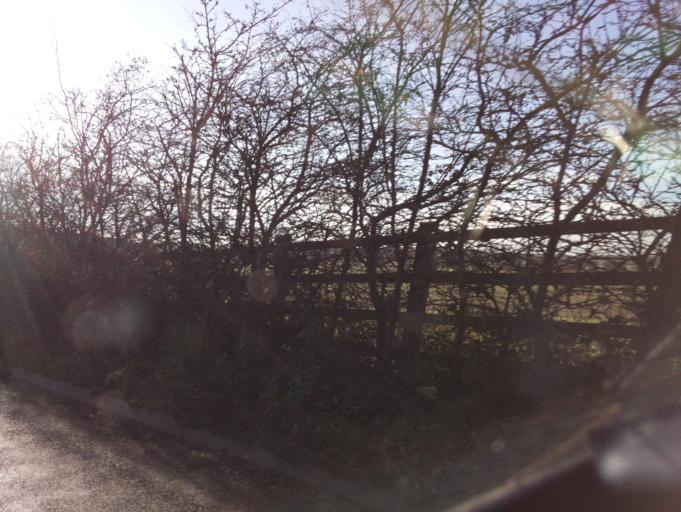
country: GB
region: England
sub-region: Staffordshire
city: Barton under Needwood
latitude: 52.8143
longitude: -1.7358
